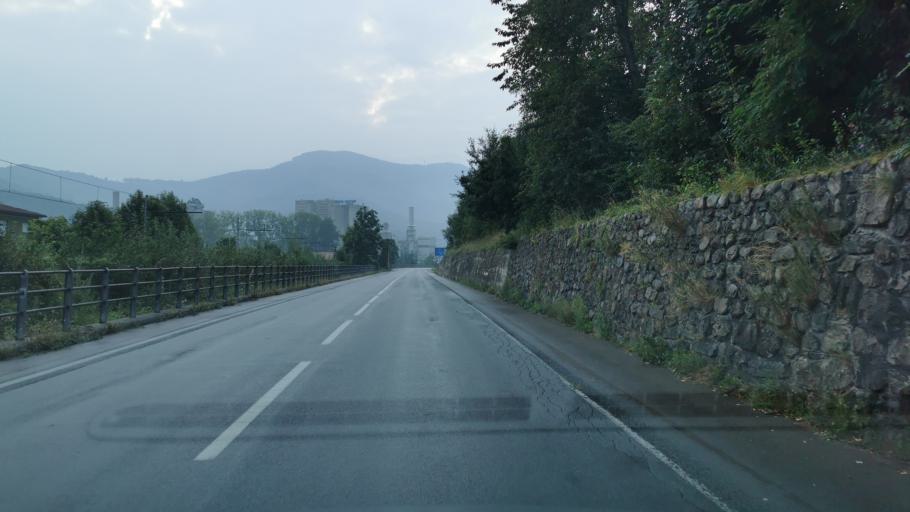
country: IT
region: Piedmont
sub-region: Provincia di Cuneo
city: Robilante
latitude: 44.3051
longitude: 7.4997
